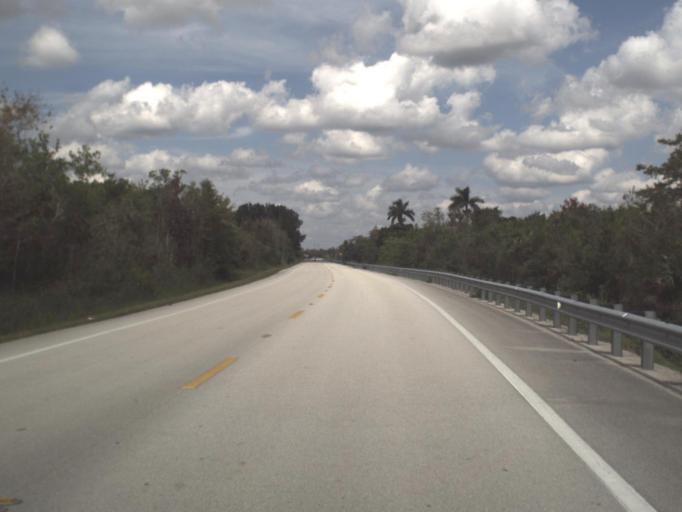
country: US
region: Florida
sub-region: Collier County
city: Lely Resort
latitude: 25.9391
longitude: -81.3572
